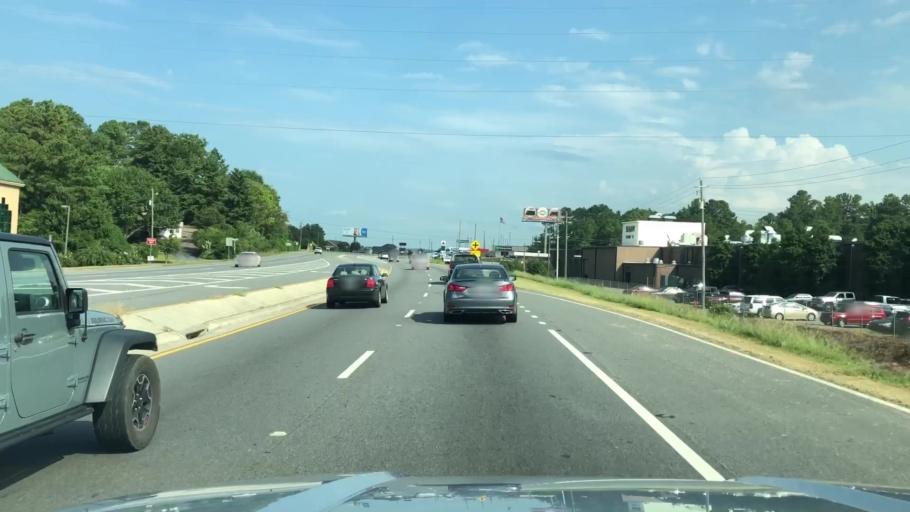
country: US
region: Georgia
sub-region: Bartow County
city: Cartersville
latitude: 34.1875
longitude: -84.7865
